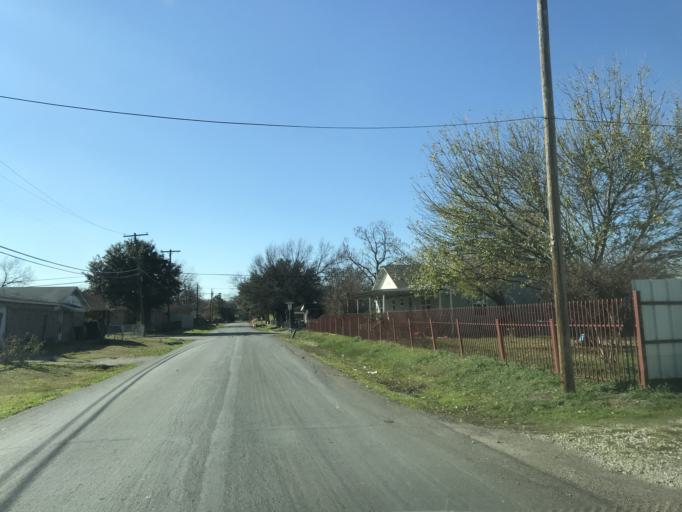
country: US
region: Texas
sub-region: Dallas County
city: Cockrell Hill
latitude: 32.7759
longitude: -96.9077
